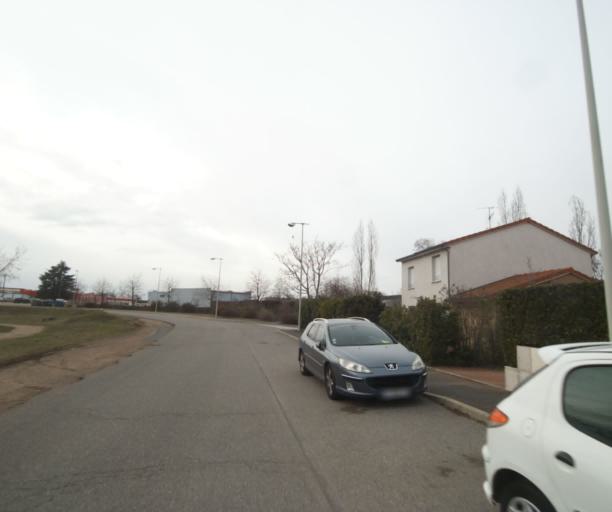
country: FR
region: Rhone-Alpes
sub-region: Departement de la Loire
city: Le Coteau
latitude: 46.0524
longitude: 4.0877
